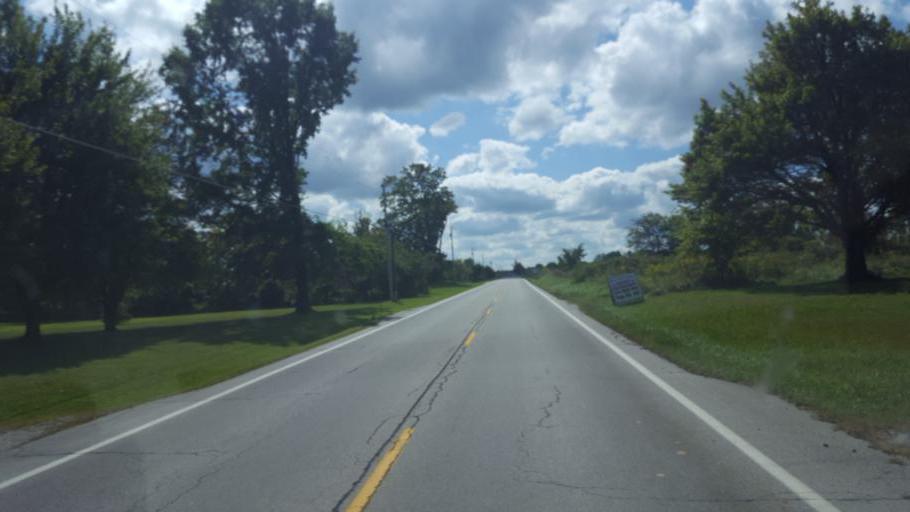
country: US
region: Ohio
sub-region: Wayne County
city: West Salem
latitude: 41.0036
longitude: -82.2227
